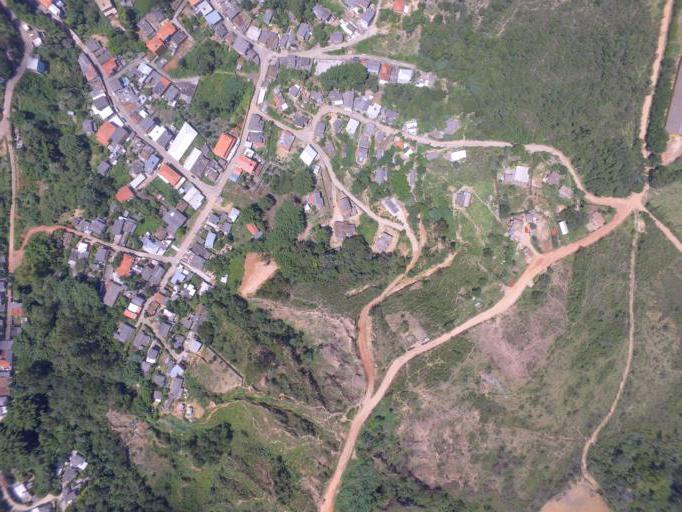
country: BR
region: Minas Gerais
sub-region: Tiradentes
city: Tiradentes
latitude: -21.0516
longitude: -44.0750
